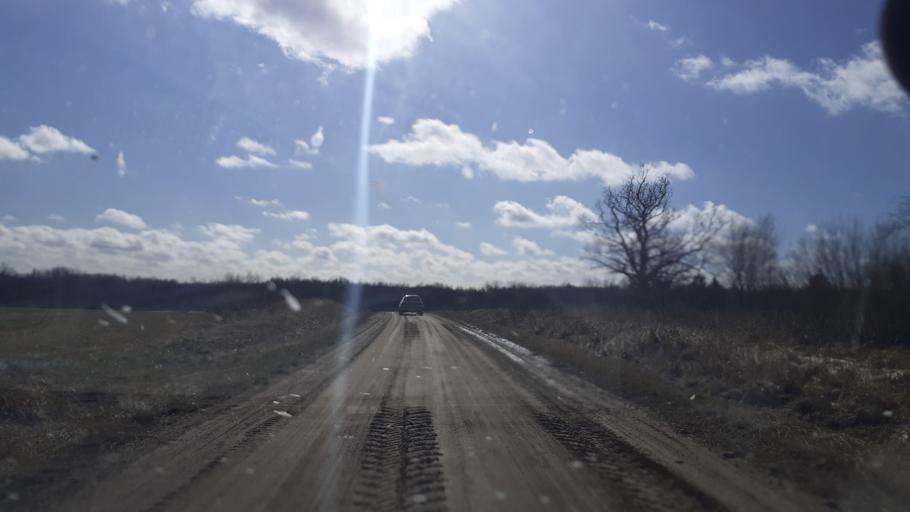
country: LV
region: Kuldigas Rajons
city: Kuldiga
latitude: 56.9280
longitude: 22.1512
